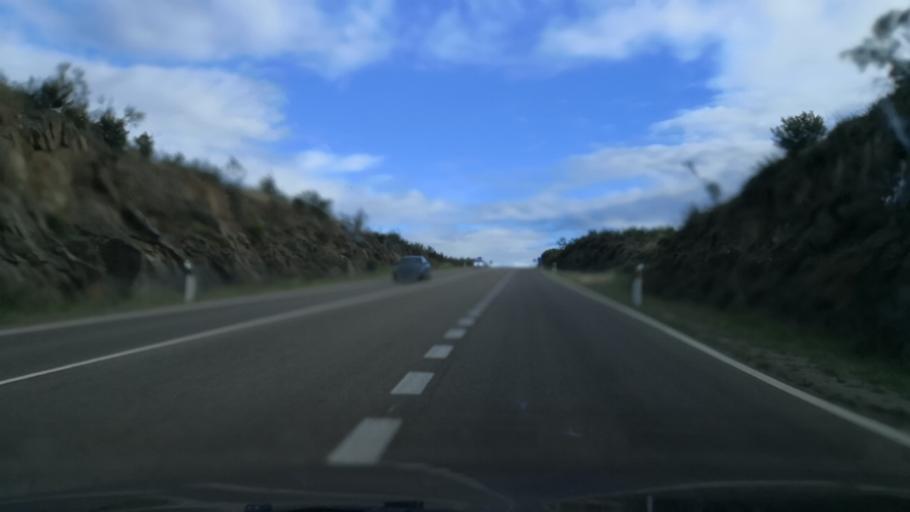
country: ES
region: Extremadura
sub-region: Provincia de Caceres
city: Coria
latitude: 39.9482
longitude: -6.5086
